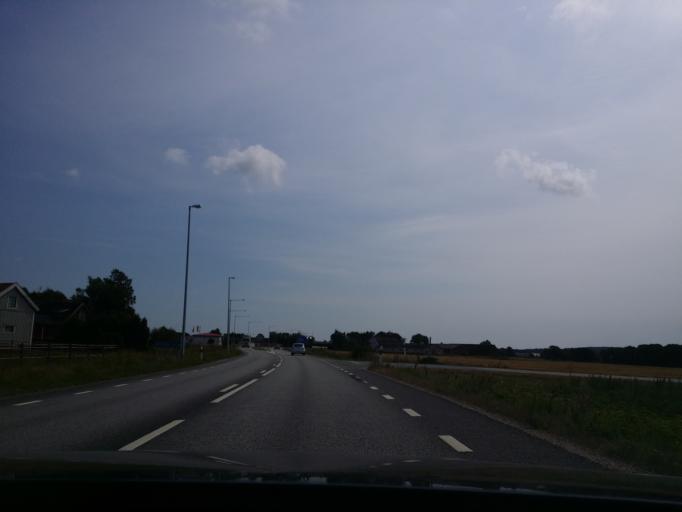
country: SE
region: Blekinge
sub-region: Solvesborgs Kommun
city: Soelvesborg
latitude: 56.0457
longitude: 14.6634
